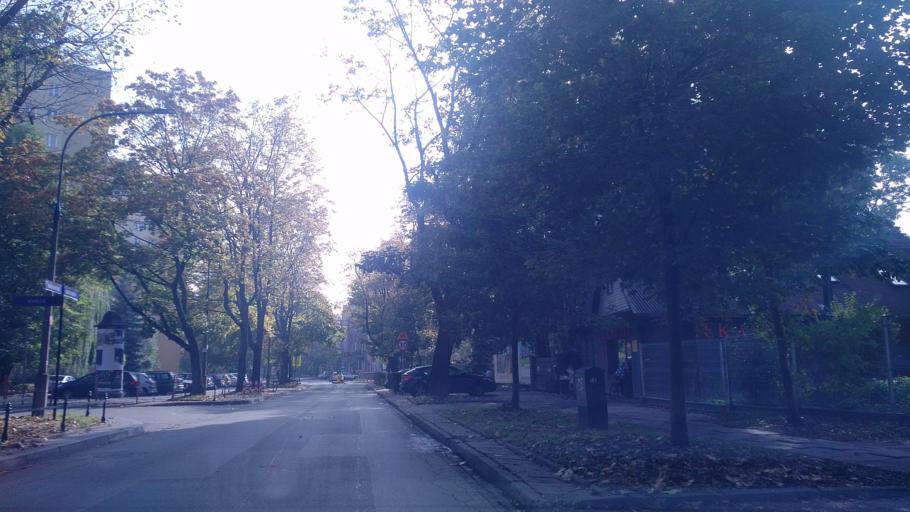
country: PL
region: Lesser Poland Voivodeship
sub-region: Krakow
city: Krakow
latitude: 50.0767
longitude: 19.9216
